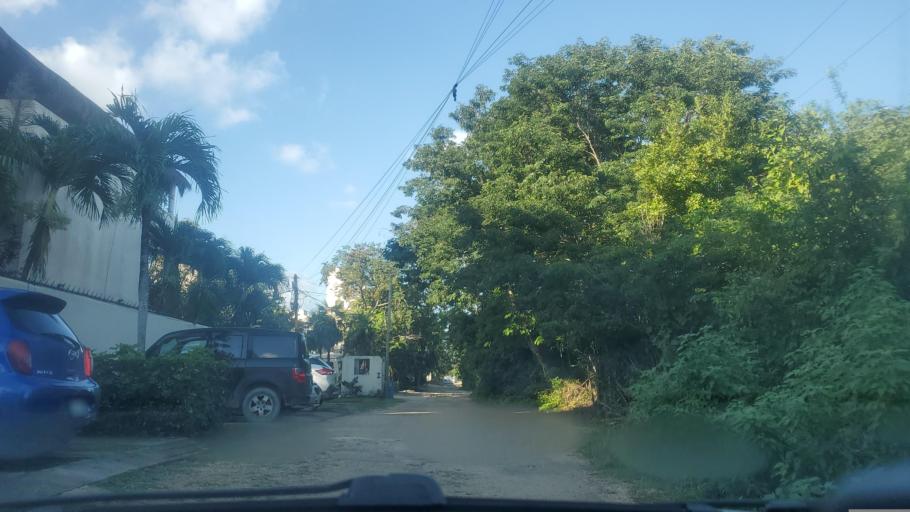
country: MX
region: Quintana Roo
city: Tulum
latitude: 20.2079
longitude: -87.4766
